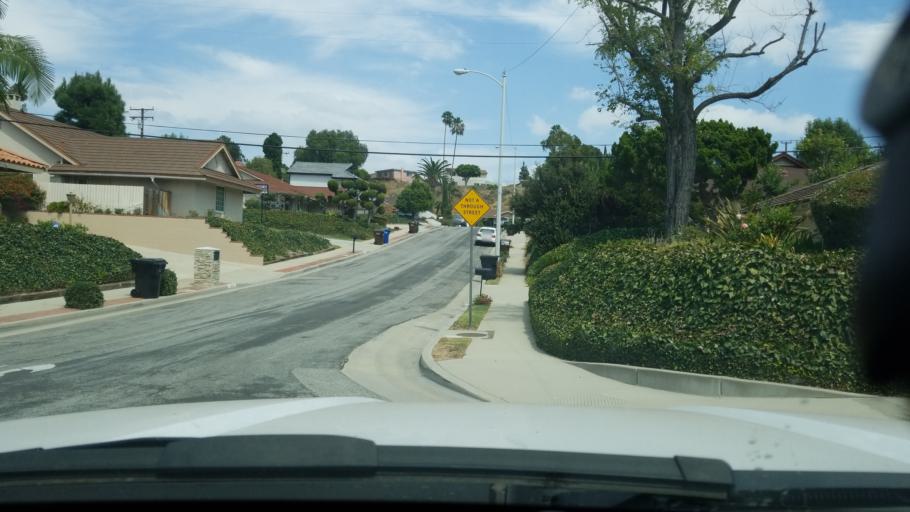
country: US
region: California
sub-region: Los Angeles County
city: Hacienda Heights
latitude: 33.9850
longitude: -117.9589
